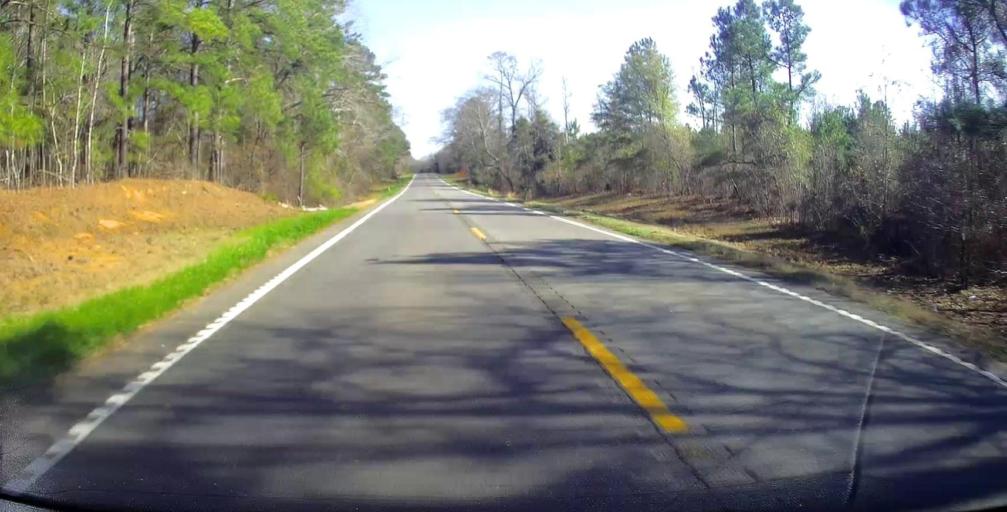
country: US
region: Georgia
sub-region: Macon County
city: Oglethorpe
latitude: 32.3416
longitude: -84.1327
